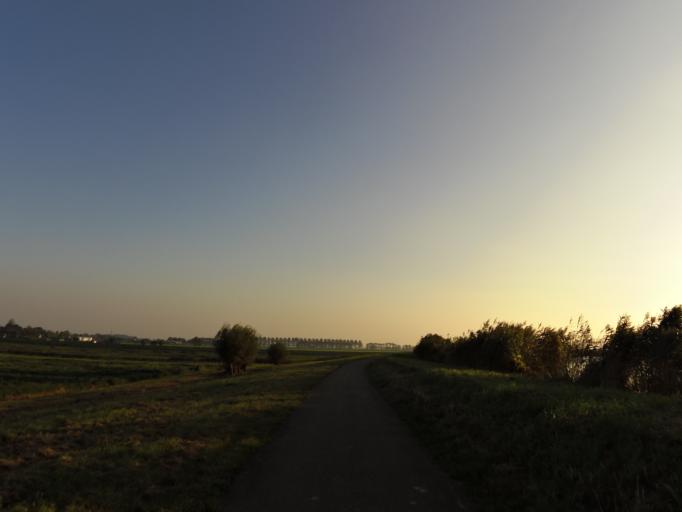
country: NL
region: South Holland
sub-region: Gemeente Kaag en Braassem
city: Oude Wetering
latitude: 52.1753
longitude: 4.6181
